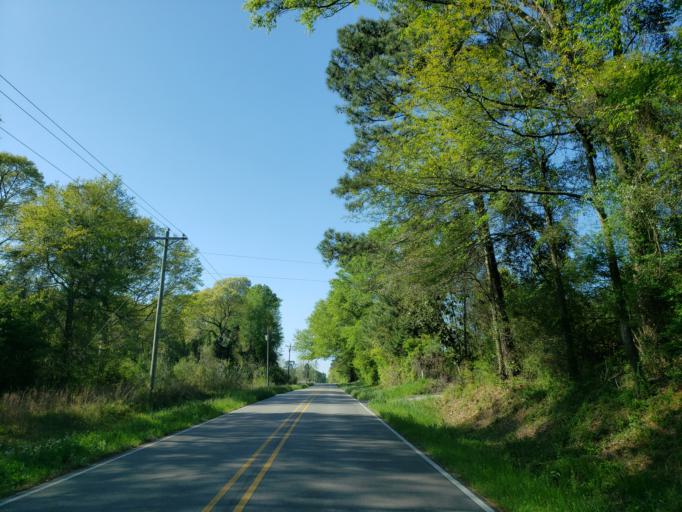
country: US
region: Mississippi
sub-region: Jones County
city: Ellisville
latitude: 31.5722
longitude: -89.3706
